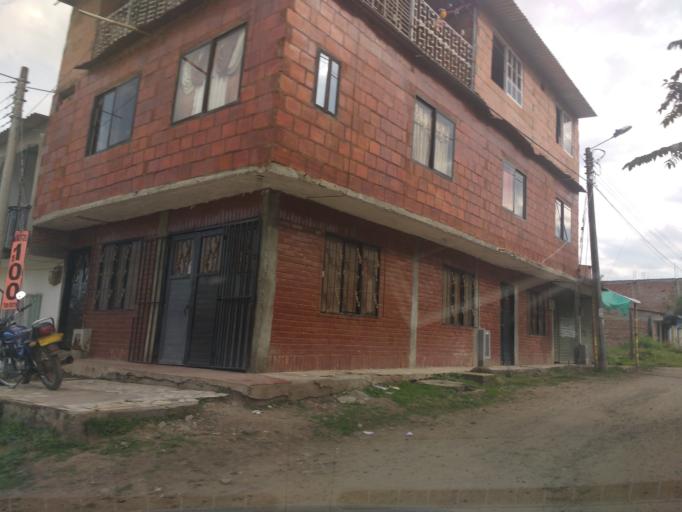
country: CO
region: Cauca
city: Miranda
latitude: 3.2568
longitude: -76.2317
